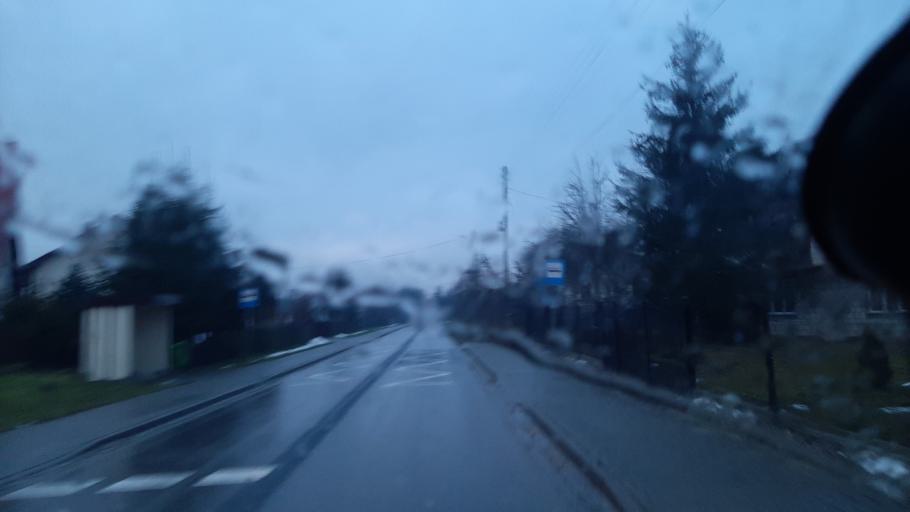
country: PL
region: Lublin Voivodeship
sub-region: Powiat lubartowski
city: Ostrowek
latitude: 51.5422
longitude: 22.5678
